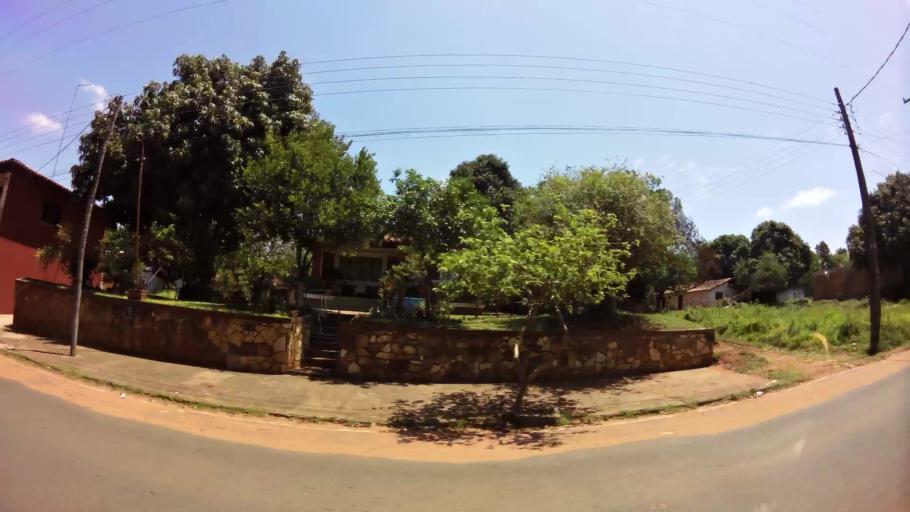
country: PY
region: Central
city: San Antonio
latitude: -25.4185
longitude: -57.5270
